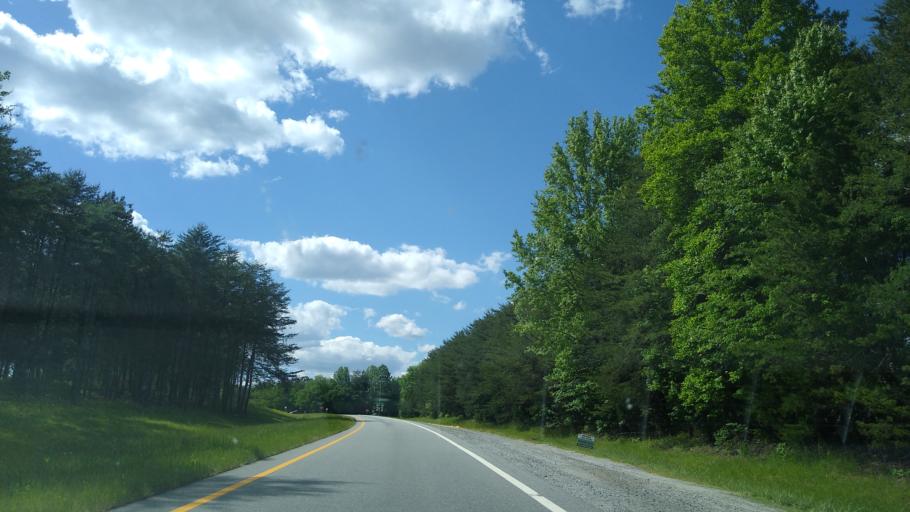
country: US
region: North Carolina
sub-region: Davidson County
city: Wallburg
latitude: 36.0264
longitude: -80.0561
